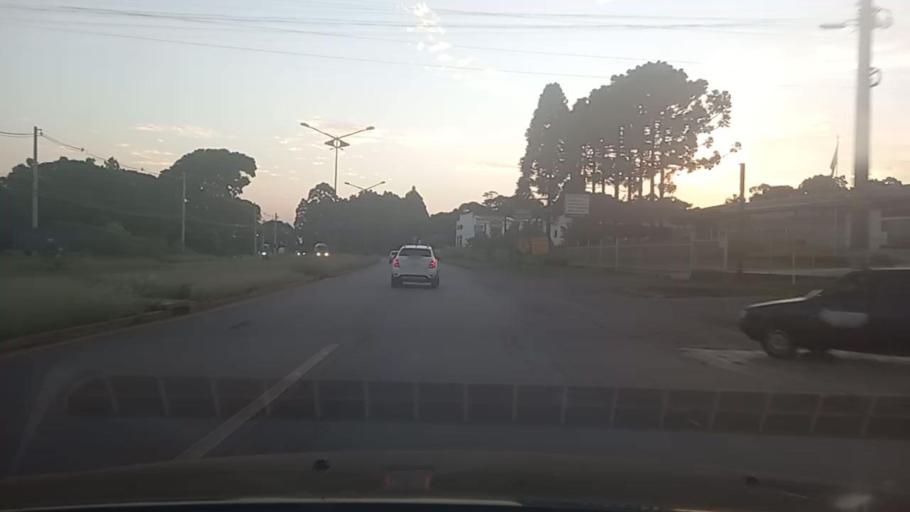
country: BR
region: Rio Grande do Sul
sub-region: Passo Fundo
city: Passo Fundo
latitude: -28.2740
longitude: -52.4466
